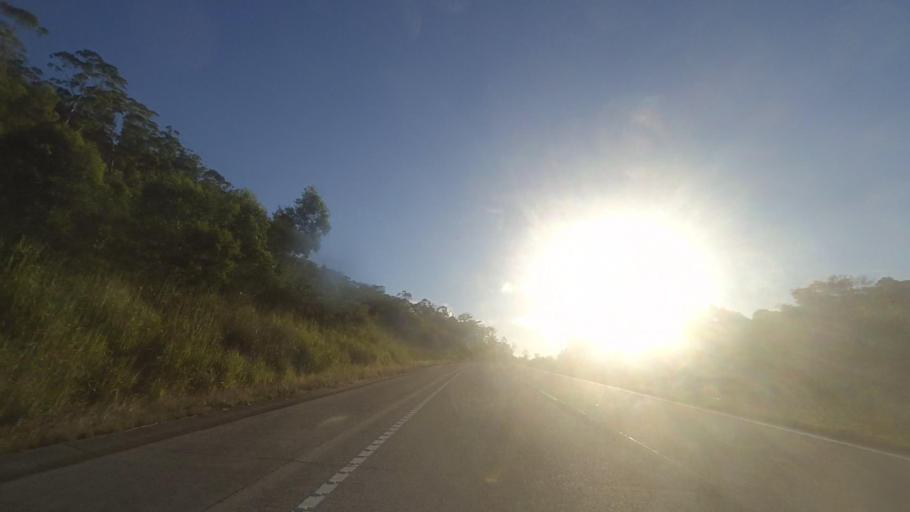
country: AU
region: New South Wales
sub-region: Great Lakes
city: Bulahdelah
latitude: -32.5340
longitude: 152.1803
